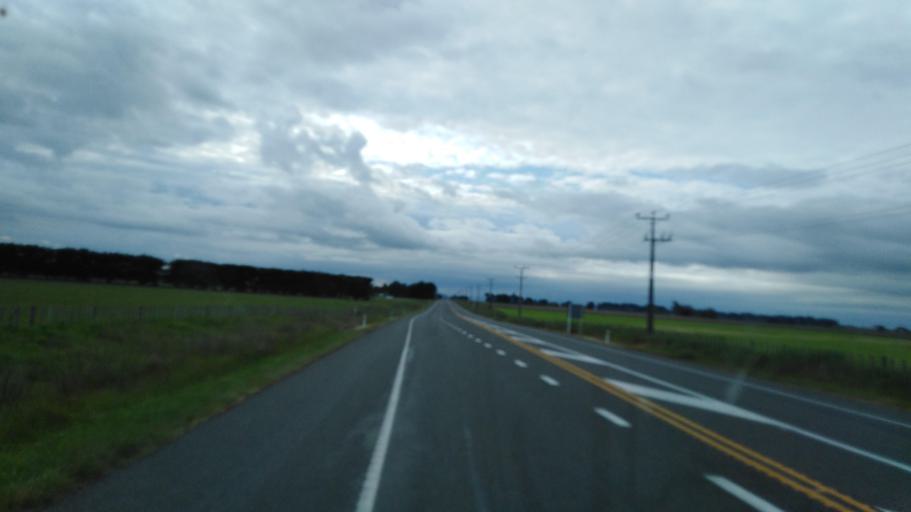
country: NZ
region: Manawatu-Wanganui
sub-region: Rangitikei District
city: Bulls
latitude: -40.1258
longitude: 175.3546
